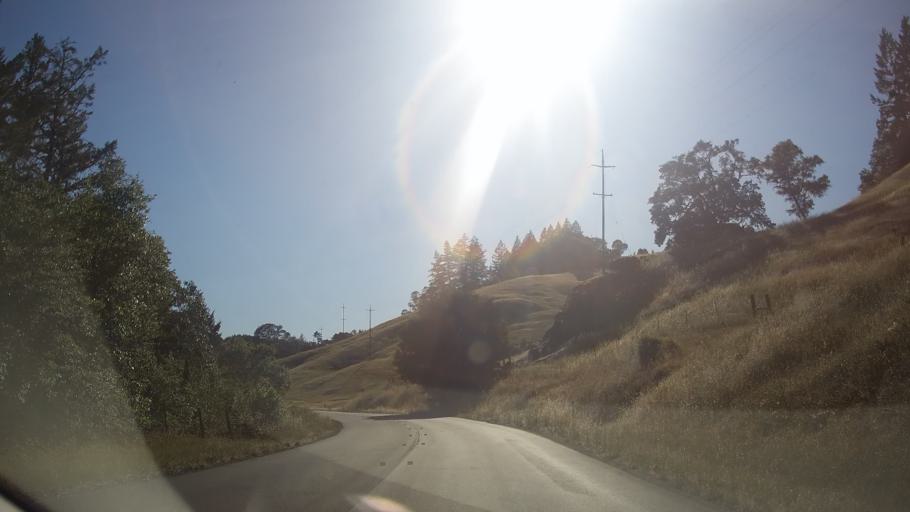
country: US
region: California
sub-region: Mendocino County
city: Willits
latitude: 39.3926
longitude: -123.4016
